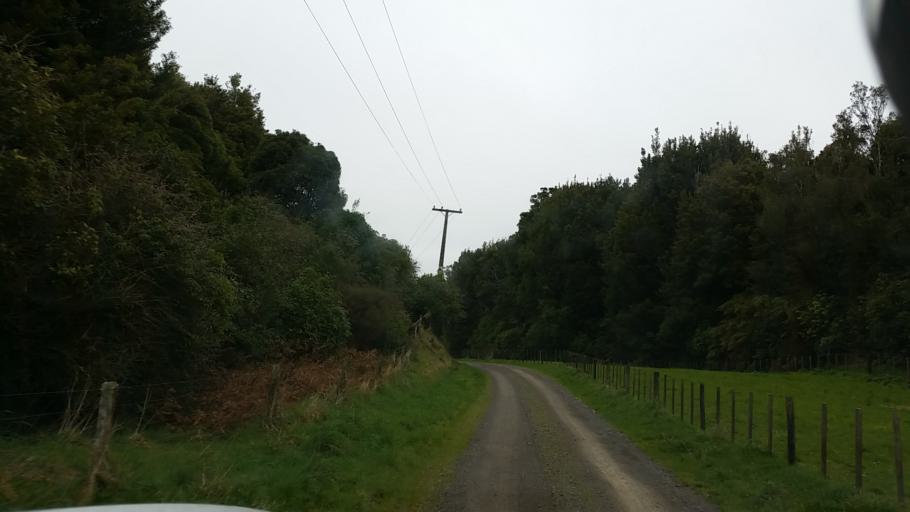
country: NZ
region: Bay of Plenty
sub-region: Rotorua District
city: Rotorua
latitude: -38.1014
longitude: 176.0678
